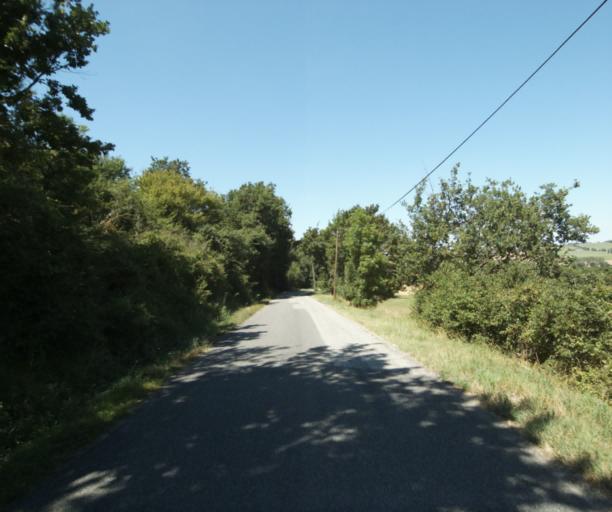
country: FR
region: Midi-Pyrenees
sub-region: Departement de la Haute-Garonne
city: Saint-Felix-Lauragais
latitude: 43.4801
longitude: 1.8701
